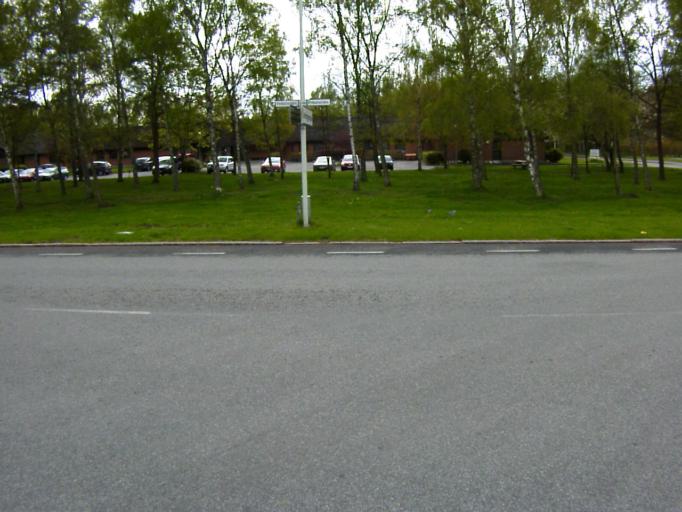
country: SE
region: Skane
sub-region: Kristianstads Kommun
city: Kristianstad
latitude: 56.0403
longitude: 14.1766
